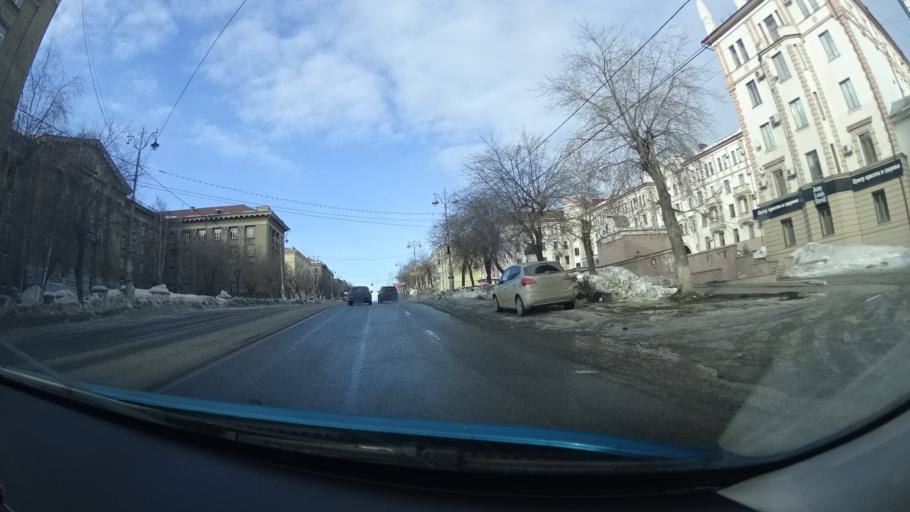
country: RU
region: Chelyabinsk
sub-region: Gorod Magnitogorsk
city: Magnitogorsk
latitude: 53.4266
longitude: 58.9836
